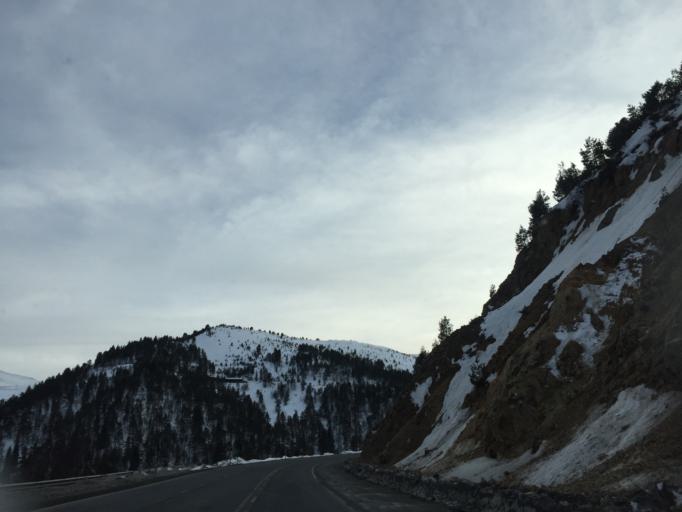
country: TR
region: Gumushane
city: Yaglidere
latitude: 40.6601
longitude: 39.4139
